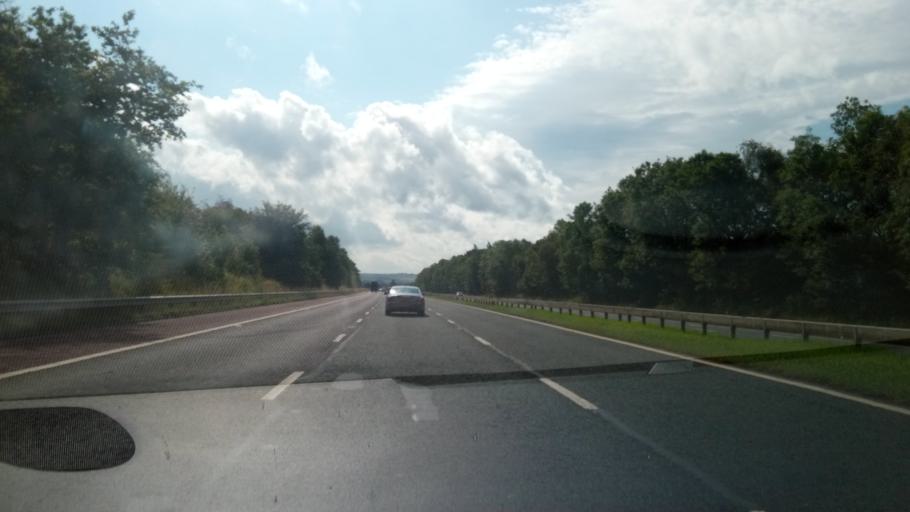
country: GB
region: England
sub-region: Cumbria
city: Penrith
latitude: 54.7632
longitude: -2.8333
